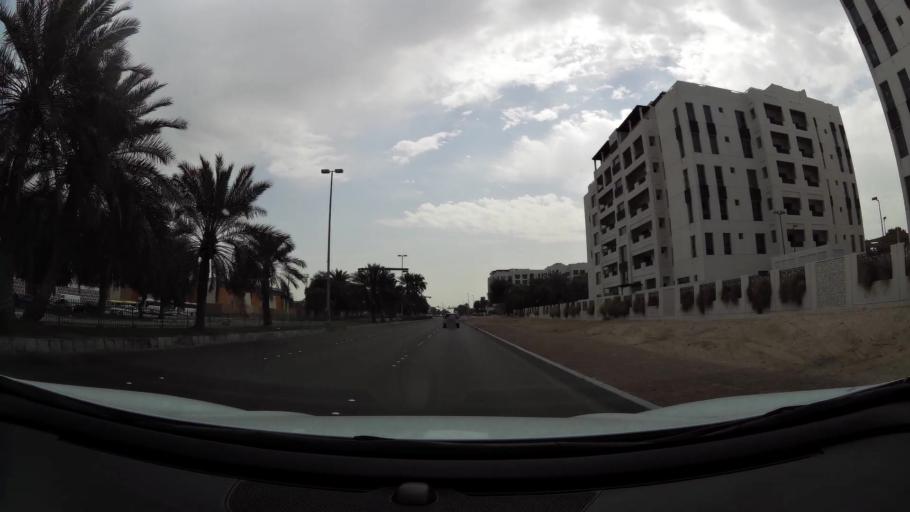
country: AE
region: Abu Dhabi
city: Abu Dhabi
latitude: 24.4587
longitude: 54.3532
